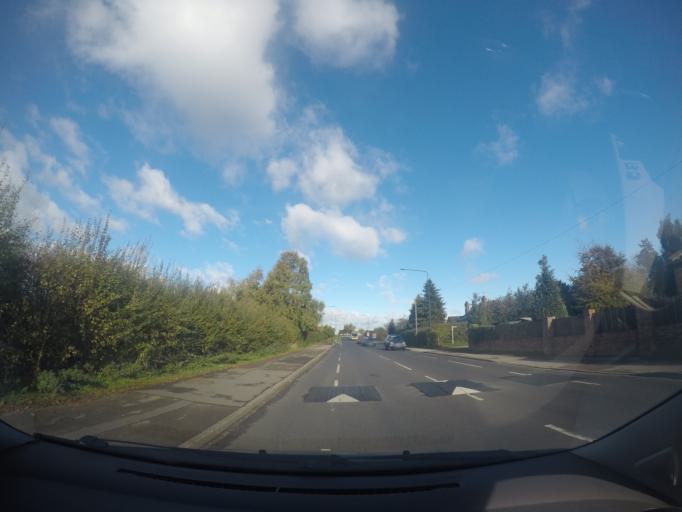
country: GB
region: England
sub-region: City of York
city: Haxby
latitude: 53.9993
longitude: -1.0726
